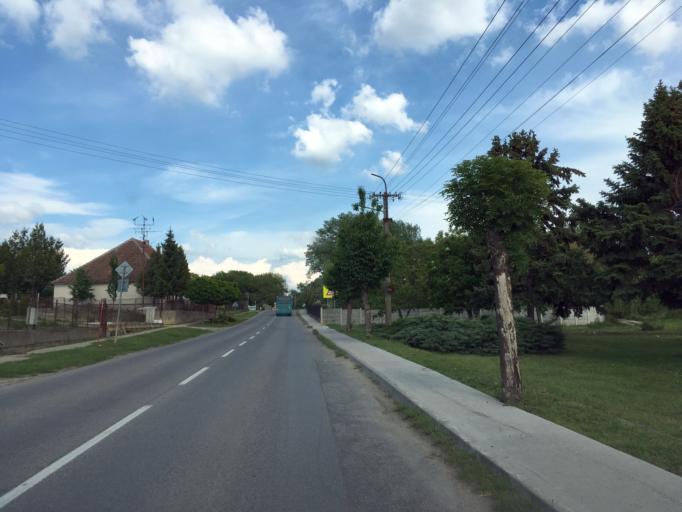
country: HU
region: Komarom-Esztergom
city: Almasfuzito
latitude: 47.7904
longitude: 18.2859
